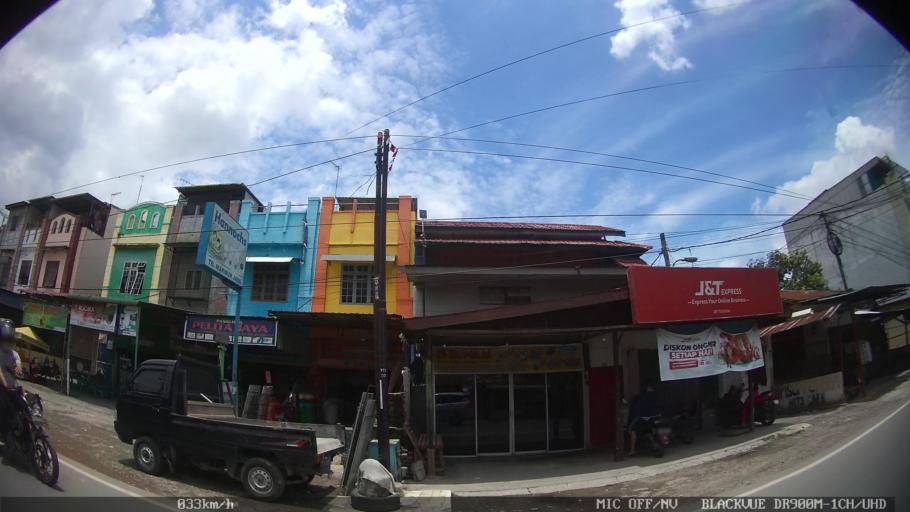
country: ID
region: North Sumatra
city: Medan
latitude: 3.6162
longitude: 98.6966
